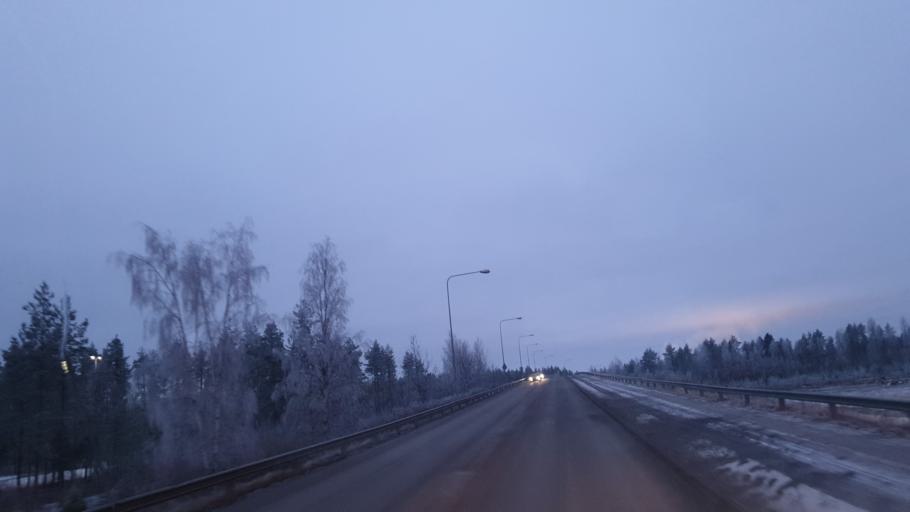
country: FI
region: Southern Ostrobothnia
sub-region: Seinaejoki
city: Nurmo
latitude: 62.7760
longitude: 22.8914
